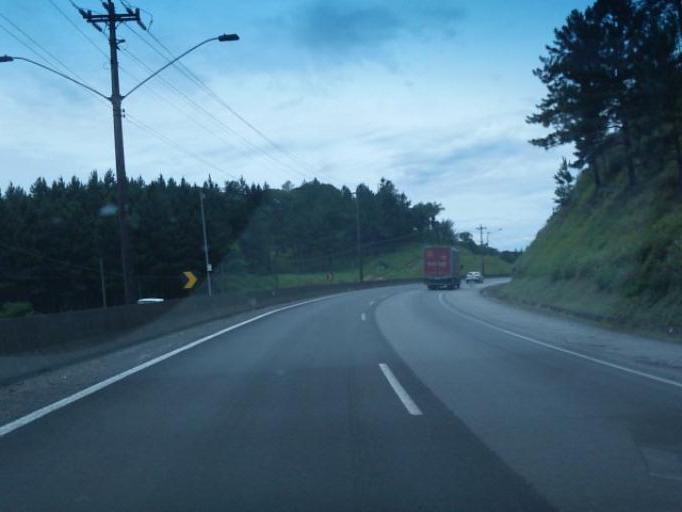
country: BR
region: Sao Paulo
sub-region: Sao Lourenco Da Serra
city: Sao Lourenco da Serra
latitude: -23.9141
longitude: -46.9892
